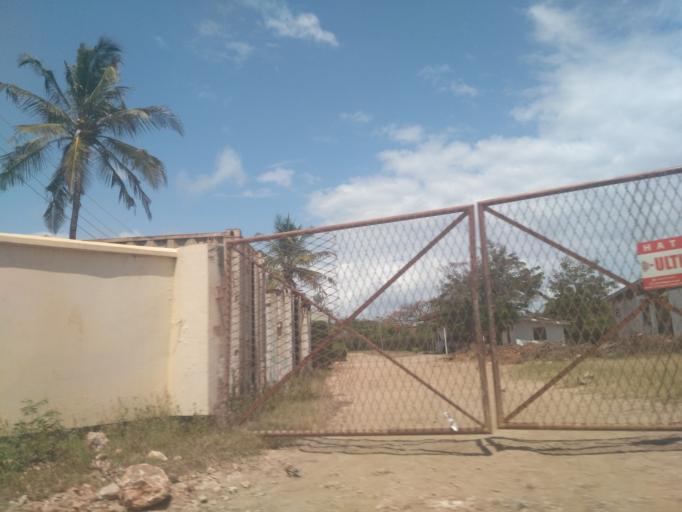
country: TZ
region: Dar es Salaam
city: Magomeni
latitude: -6.7394
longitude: 39.2829
